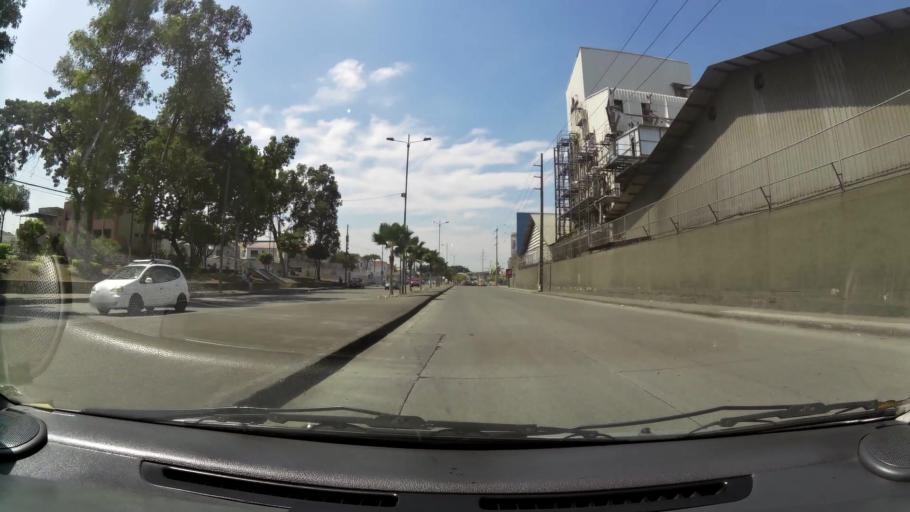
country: EC
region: Guayas
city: Eloy Alfaro
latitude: -2.1391
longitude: -79.9105
